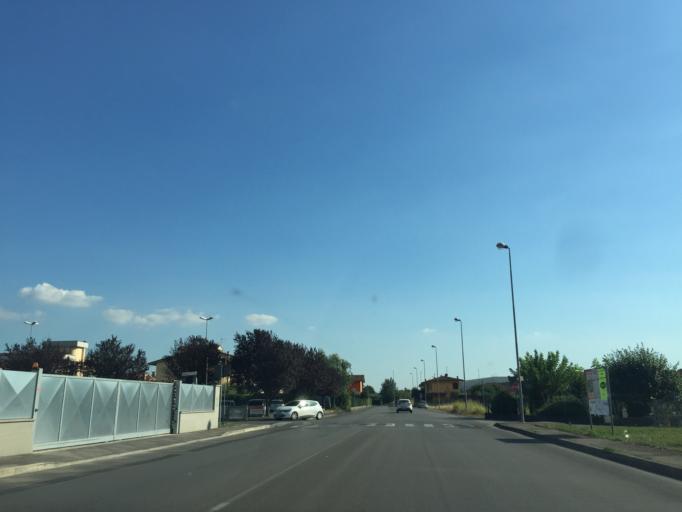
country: IT
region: Tuscany
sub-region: Provincia di Pistoia
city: Monsummano Terme
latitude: 43.8616
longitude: 10.8040
